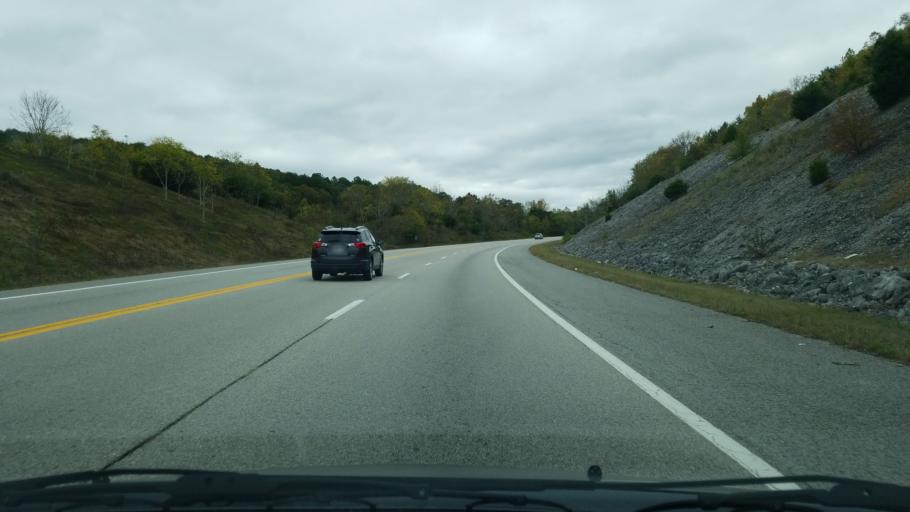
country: US
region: Tennessee
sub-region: Rhea County
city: Dayton
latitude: 35.4757
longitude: -85.0207
